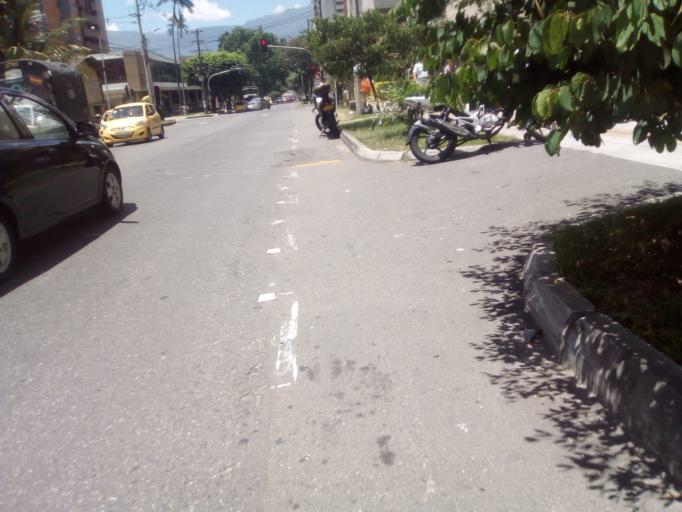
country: CO
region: Antioquia
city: Medellin
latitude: 6.2627
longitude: -75.5883
